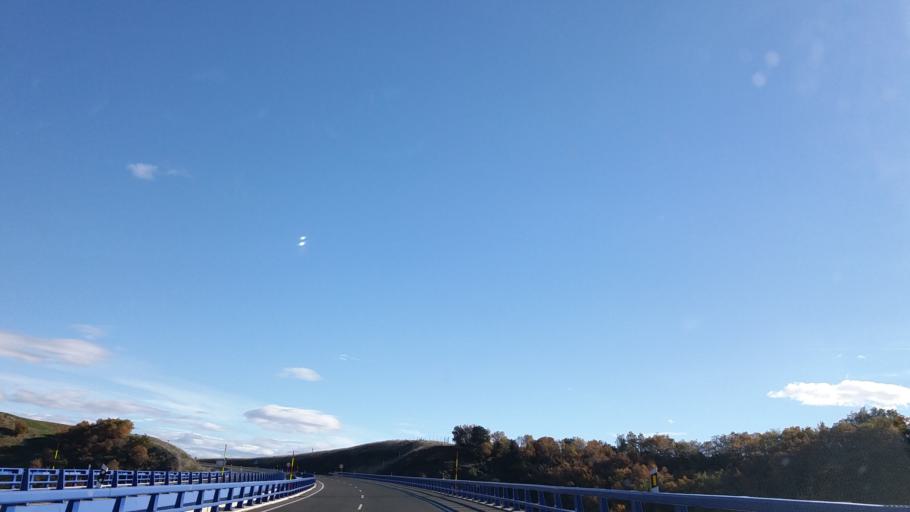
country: ES
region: Aragon
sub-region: Provincia de Zaragoza
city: Mianos
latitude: 42.6108
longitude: -0.9240
